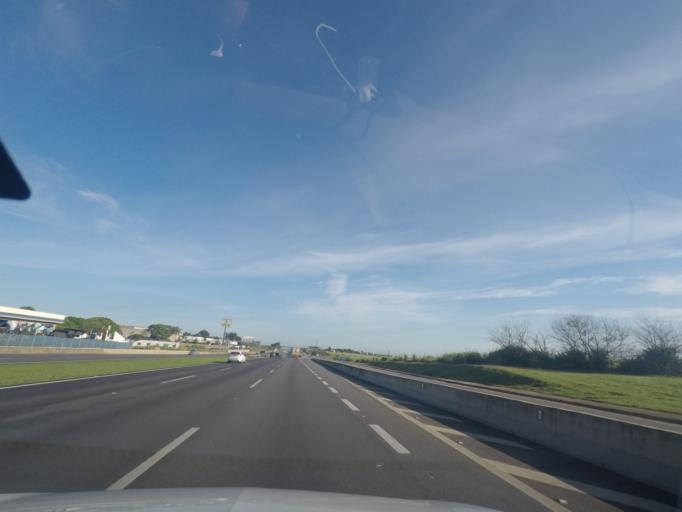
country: BR
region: Sao Paulo
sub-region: Sumare
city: Sumare
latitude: -22.7882
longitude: -47.2281
